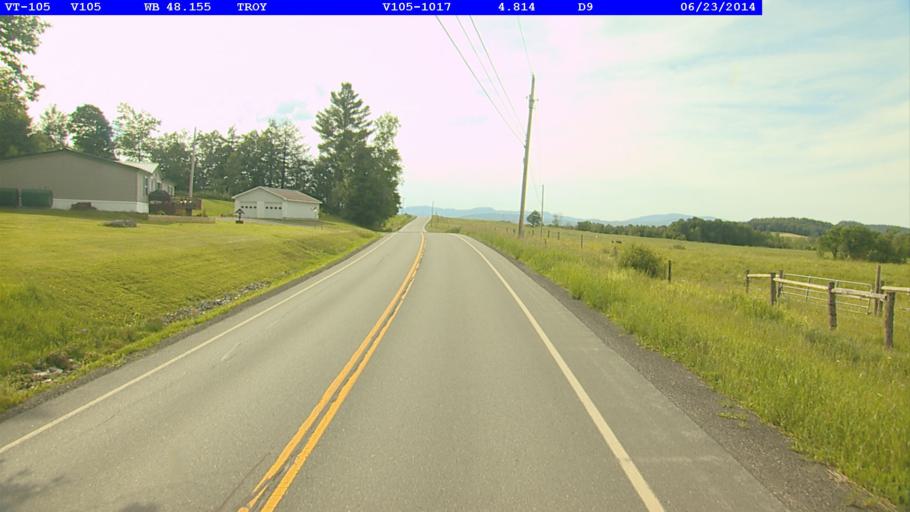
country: US
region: Vermont
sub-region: Orleans County
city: Newport
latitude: 44.9865
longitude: -72.3632
